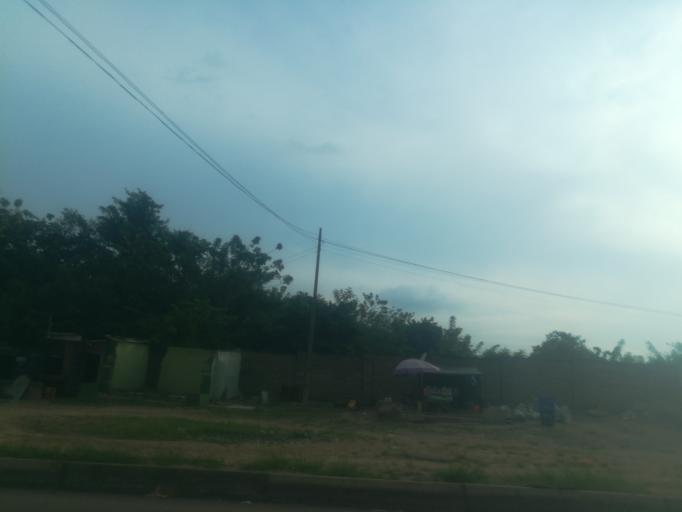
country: NG
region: Ogun
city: Abeokuta
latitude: 7.1623
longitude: 3.3167
